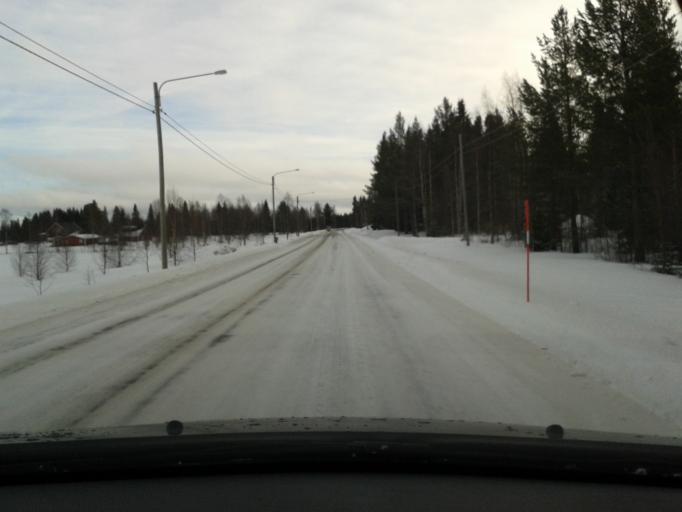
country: SE
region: Vaesterbotten
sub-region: Vilhelmina Kommun
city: Sjoberg
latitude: 64.6479
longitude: 16.3424
